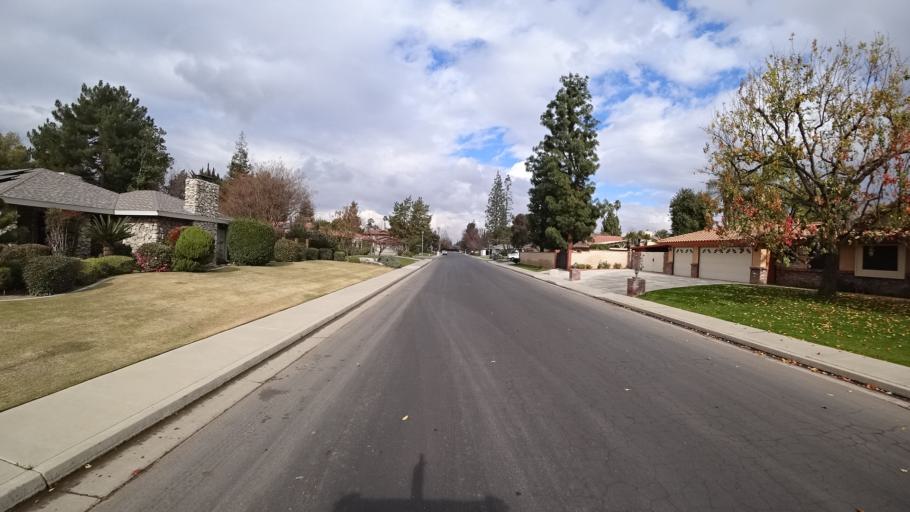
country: US
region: California
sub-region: Kern County
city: Greenacres
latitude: 35.3511
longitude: -119.0885
